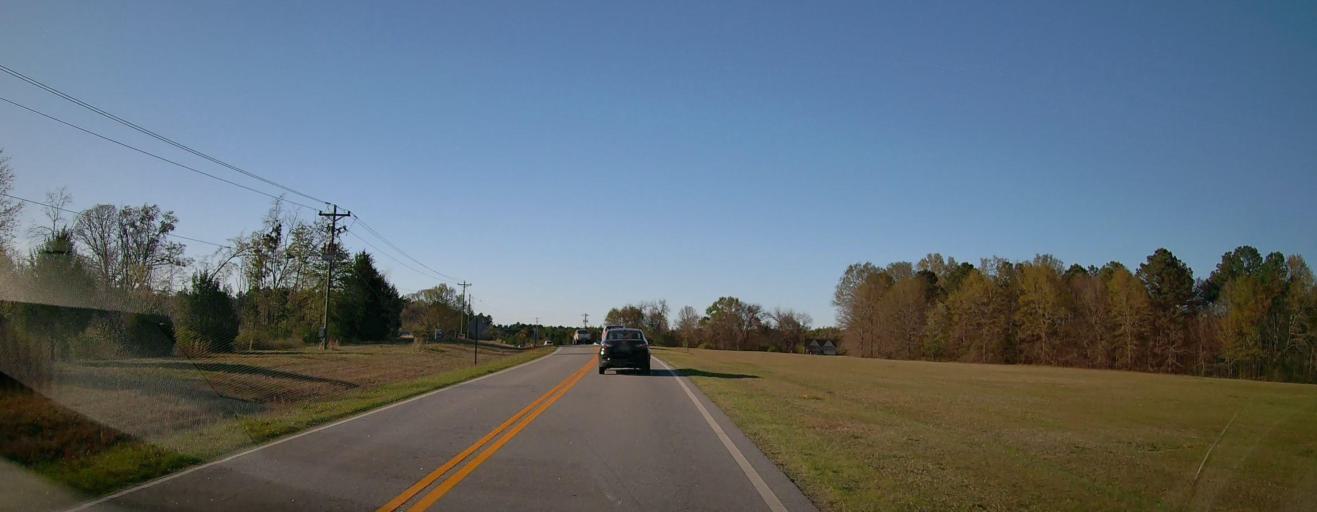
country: US
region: Georgia
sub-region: Butts County
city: Jackson
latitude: 33.3313
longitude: -83.9075
